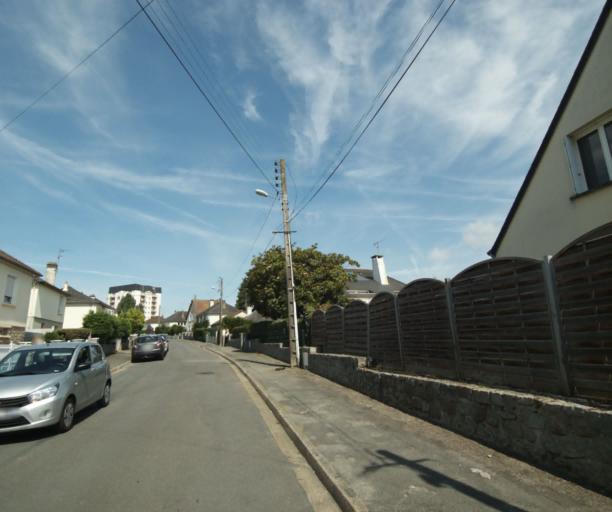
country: FR
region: Pays de la Loire
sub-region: Departement de la Mayenne
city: Laval
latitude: 48.0608
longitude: -0.7710
